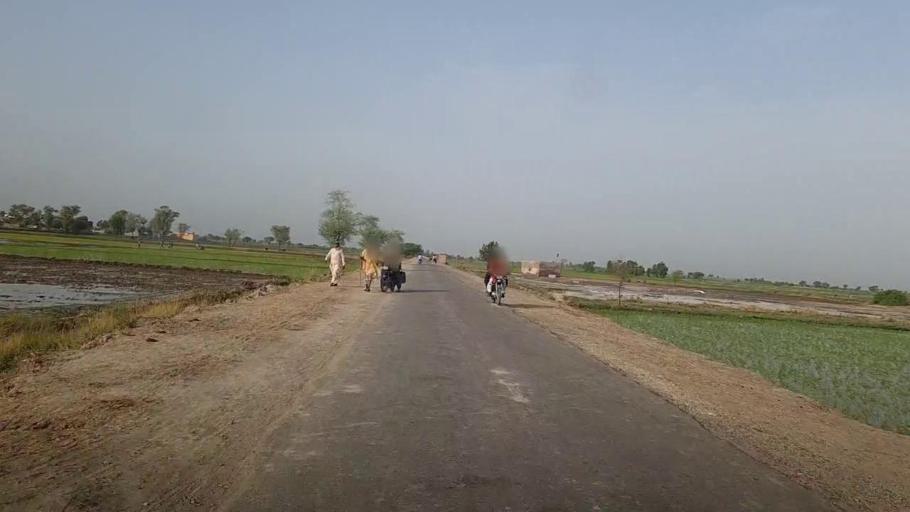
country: PK
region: Sindh
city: Mehar
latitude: 27.1574
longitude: 67.8072
